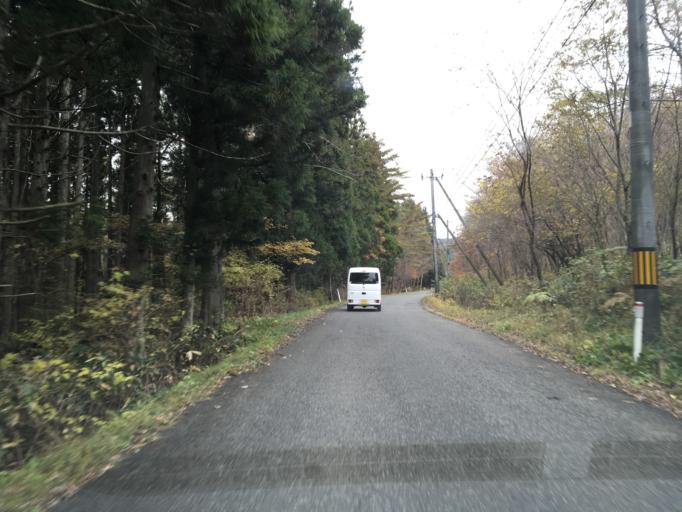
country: JP
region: Iwate
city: Mizusawa
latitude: 39.1179
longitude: 141.3236
